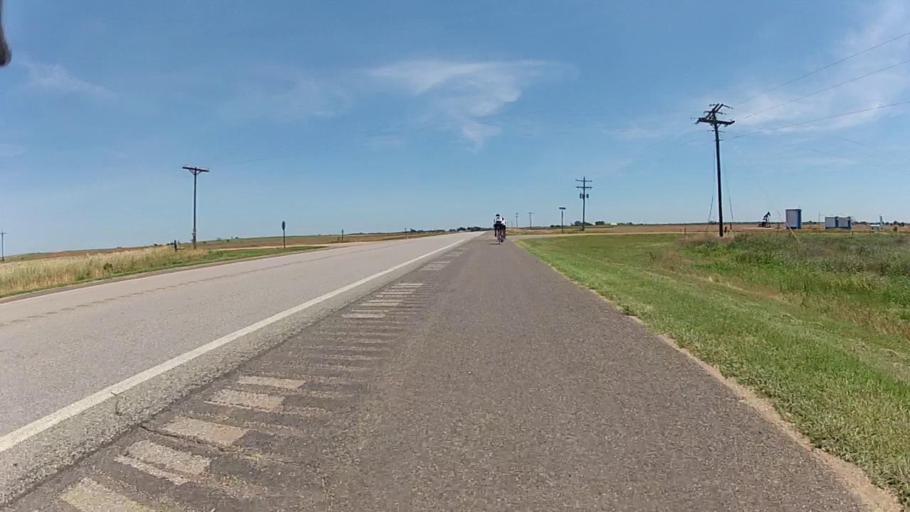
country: US
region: Kansas
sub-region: Barber County
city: Medicine Lodge
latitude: 37.2536
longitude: -98.3678
